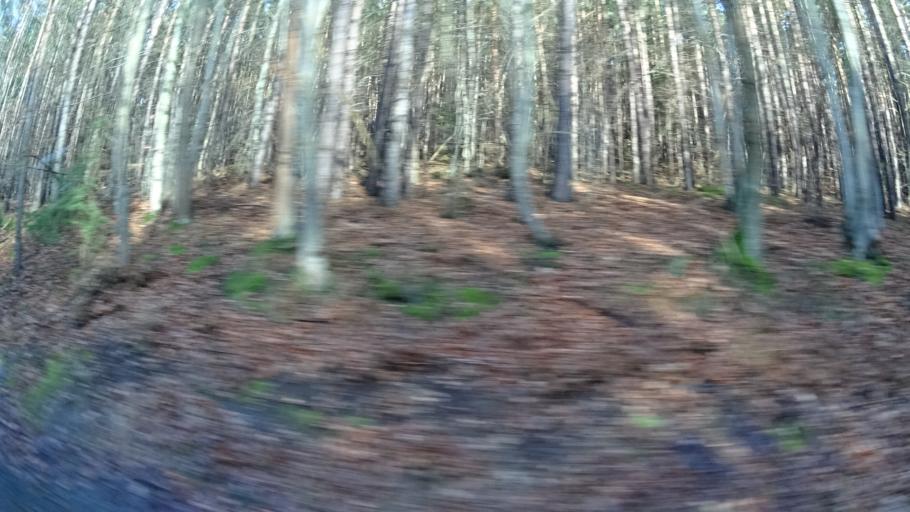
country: DE
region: Thuringia
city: Breitungen
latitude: 50.7232
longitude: 10.3027
